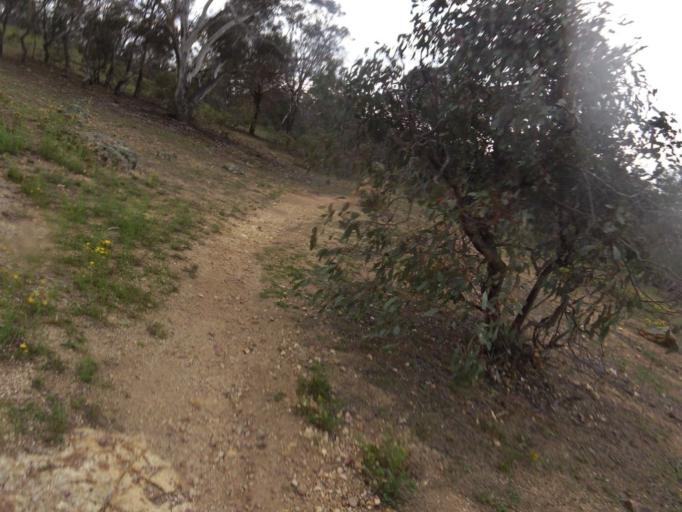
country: AU
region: Australian Capital Territory
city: Forrest
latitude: -35.3474
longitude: 149.1345
